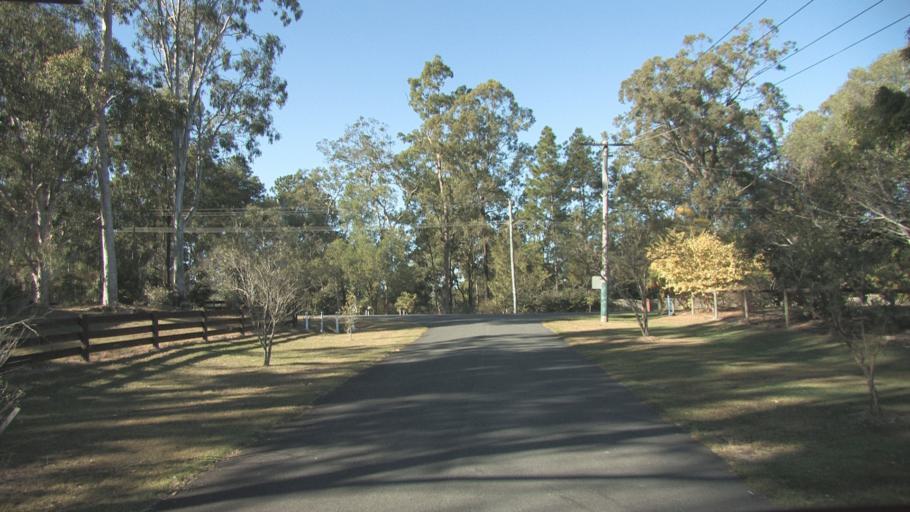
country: AU
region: Queensland
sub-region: Brisbane
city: Forest Lake
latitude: -27.6678
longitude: 153.0057
